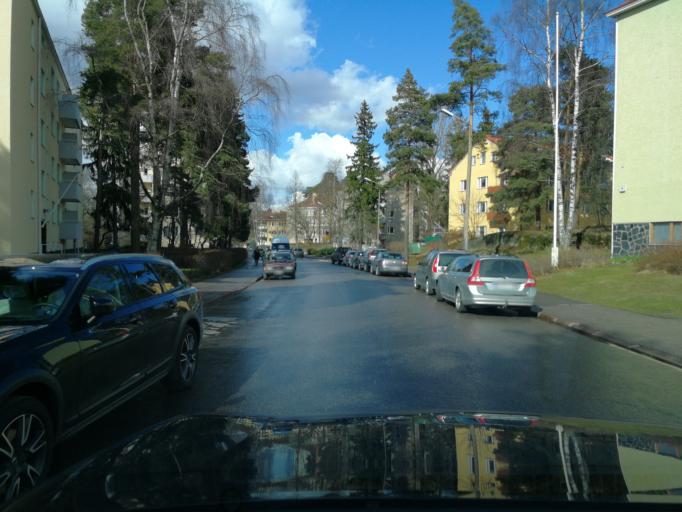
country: FI
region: Uusimaa
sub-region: Helsinki
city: Helsinki
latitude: 60.1995
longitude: 24.9049
